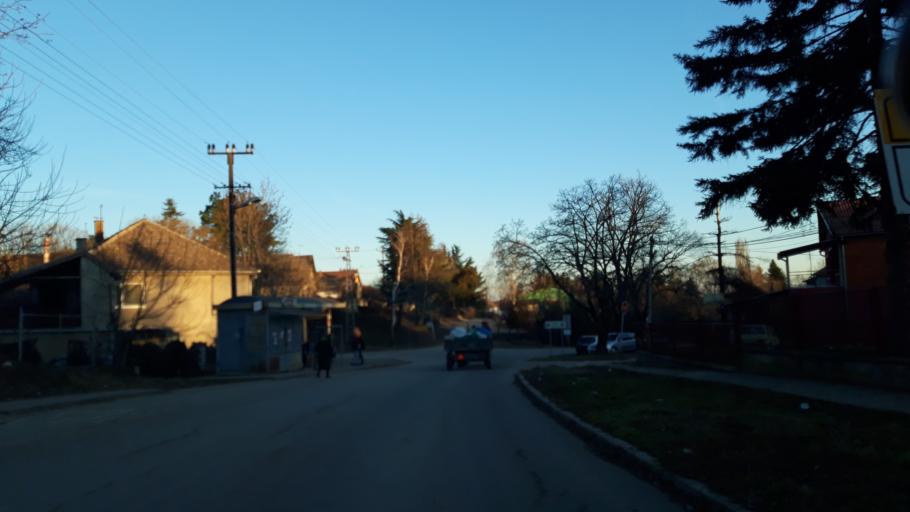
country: RS
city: Cortanovci
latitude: 45.1563
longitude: 20.0175
